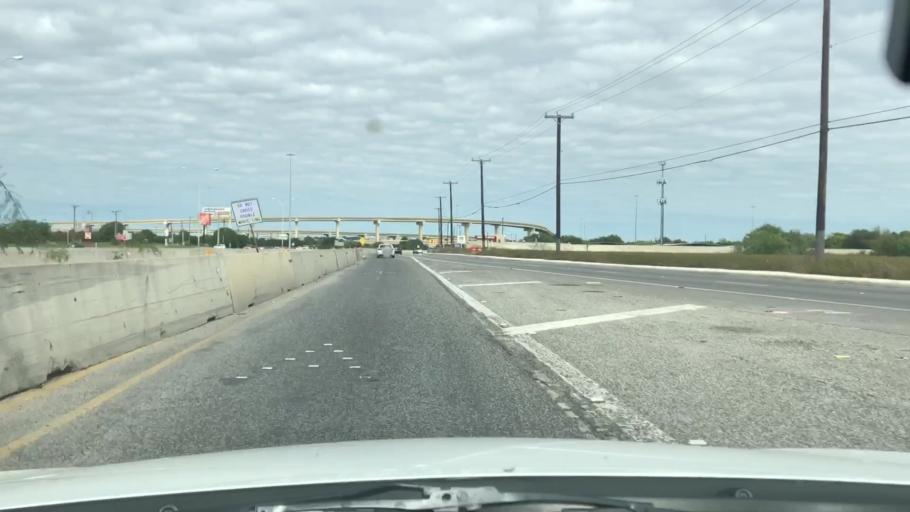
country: US
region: Texas
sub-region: Bexar County
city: Lackland Air Force Base
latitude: 29.4284
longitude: -98.6491
